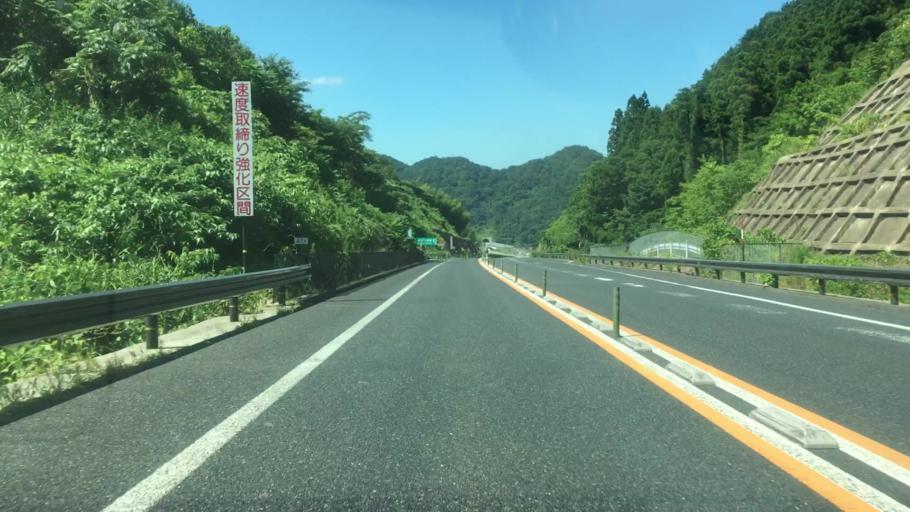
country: JP
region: Tottori
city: Tottori
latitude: 35.3687
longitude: 134.2027
